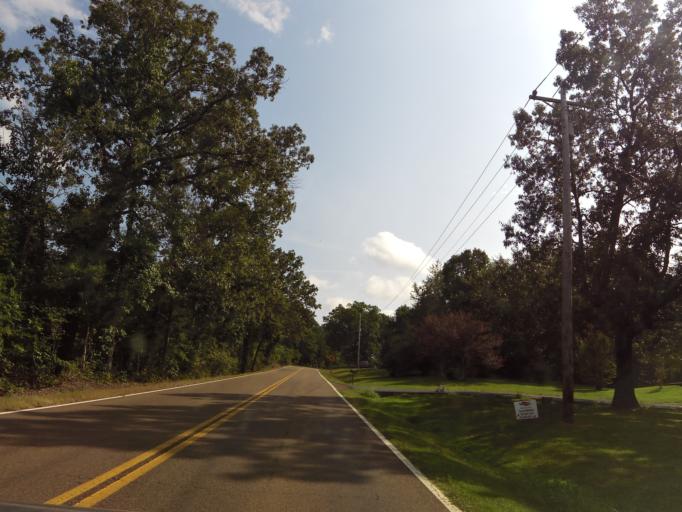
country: US
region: Tennessee
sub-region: Hardin County
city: Crump
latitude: 35.1114
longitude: -88.3678
